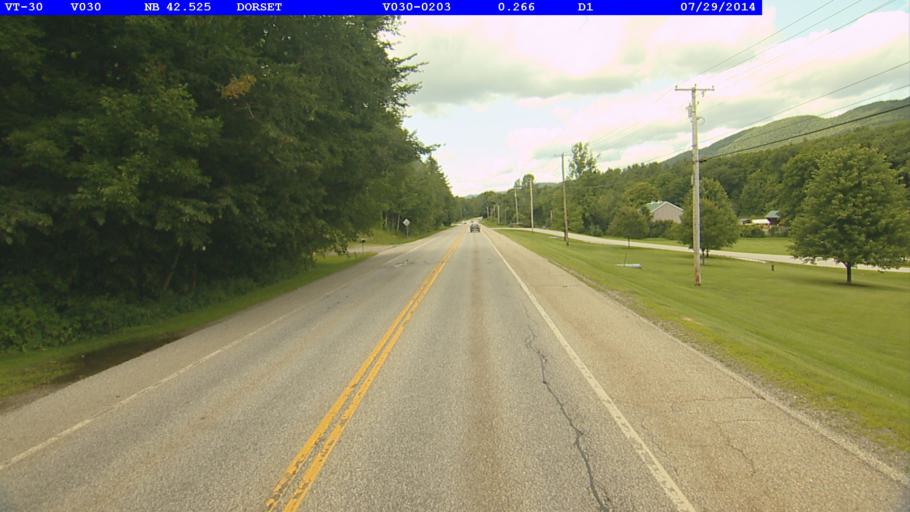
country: US
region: Vermont
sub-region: Bennington County
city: Manchester Center
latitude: 43.2161
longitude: -73.0695
